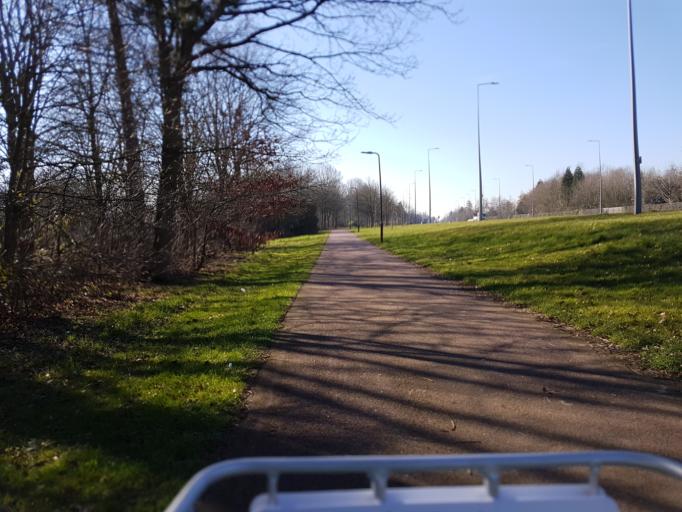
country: GB
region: England
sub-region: Buckinghamshire
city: Newton Longville
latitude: 51.9942
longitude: -0.7765
